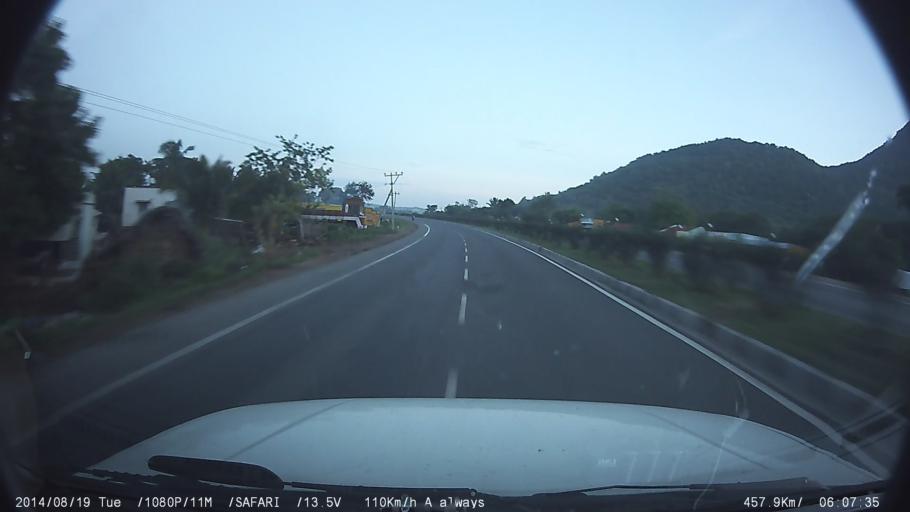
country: IN
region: Tamil Nadu
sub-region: Salem
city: Omalur
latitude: 11.9025
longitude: 78.0618
